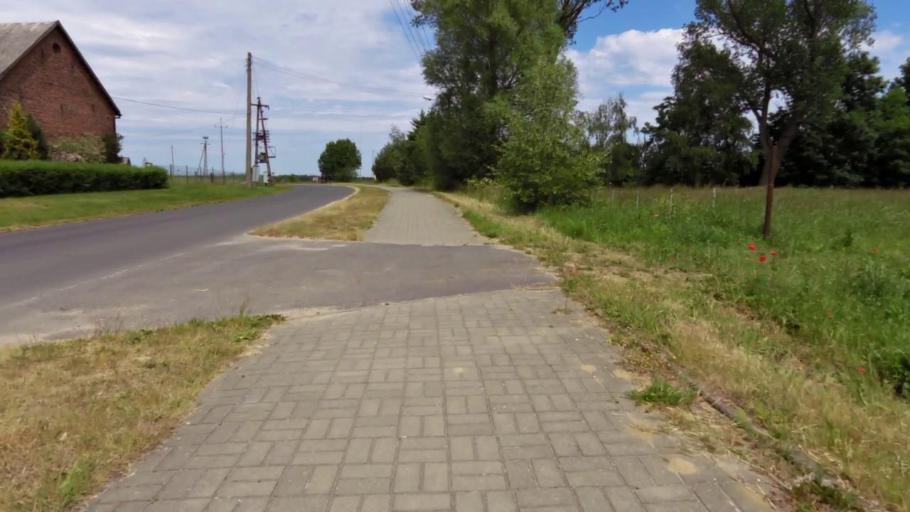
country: PL
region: West Pomeranian Voivodeship
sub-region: Powiat kamienski
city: Kamien Pomorski
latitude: 53.9827
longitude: 14.6944
